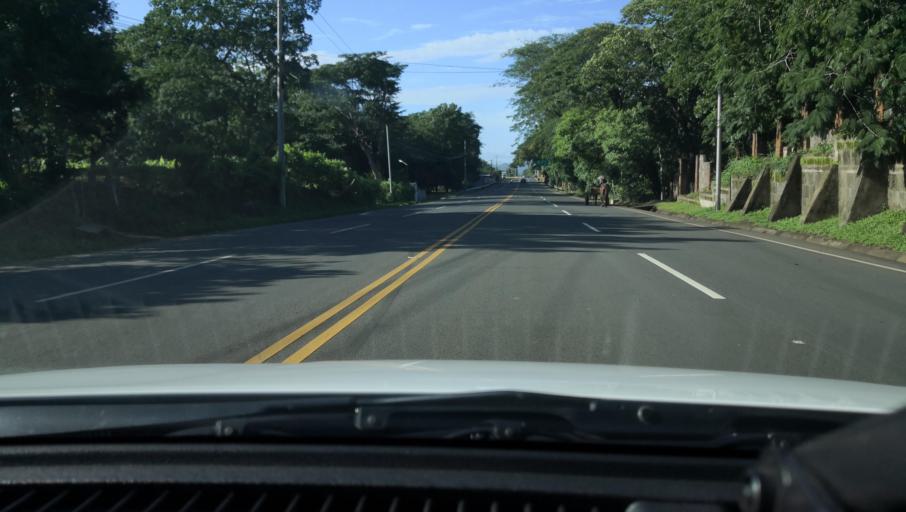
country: NI
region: Granada
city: Nandaime
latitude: 11.7812
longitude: -86.0549
